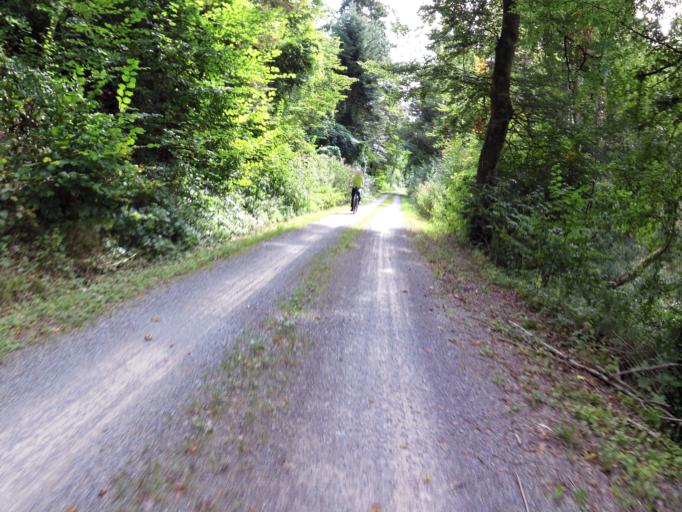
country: DE
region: Baden-Wuerttemberg
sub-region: Freiburg Region
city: Sulz am Neckar
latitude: 48.3449
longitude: 8.5951
